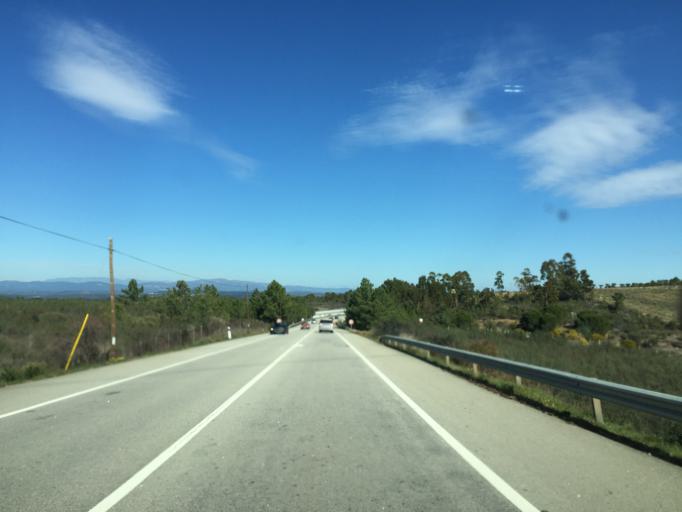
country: PT
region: Castelo Branco
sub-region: Castelo Branco
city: Castelo Branco
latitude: 39.7743
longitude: -7.5857
